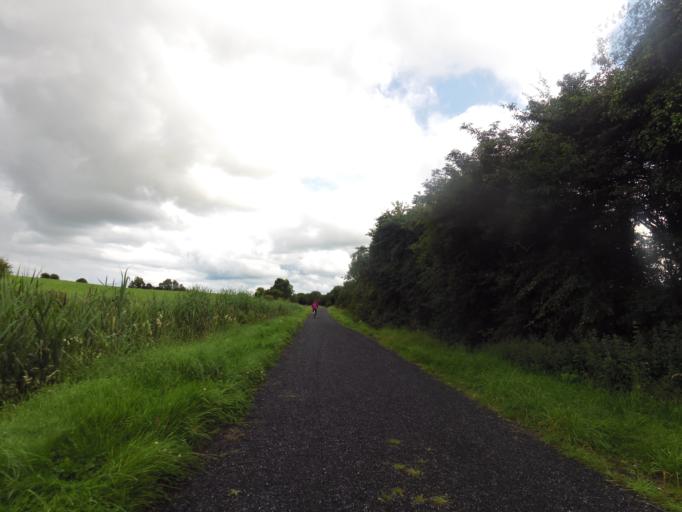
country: IE
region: Leinster
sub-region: An Iarmhi
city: An Muileann gCearr
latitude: 53.5173
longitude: -7.4336
